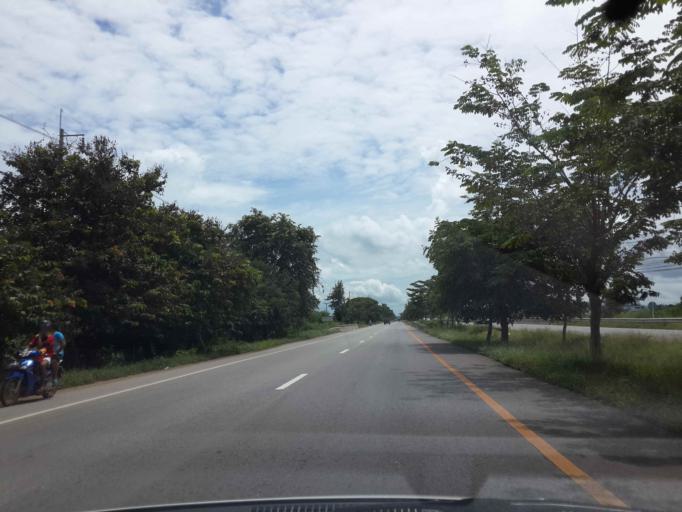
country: TH
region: Ratchaburi
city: Pak Tho
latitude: 13.3851
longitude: 99.8187
